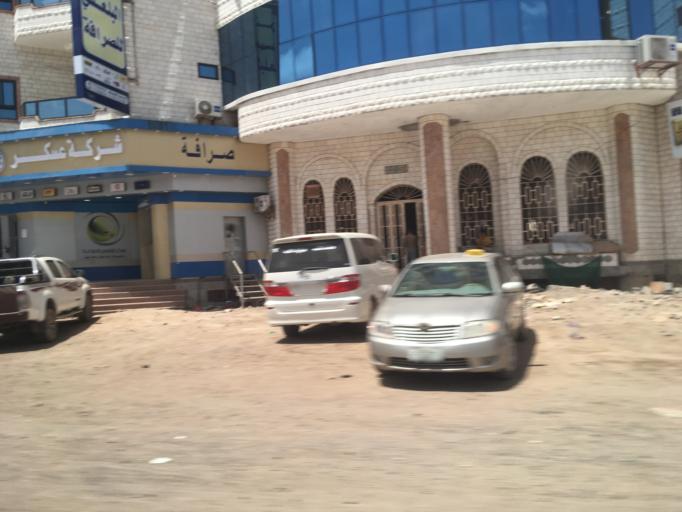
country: YE
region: Aden
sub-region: Al Mansura
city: Al Mansurah
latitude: 12.8654
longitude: 44.9710
